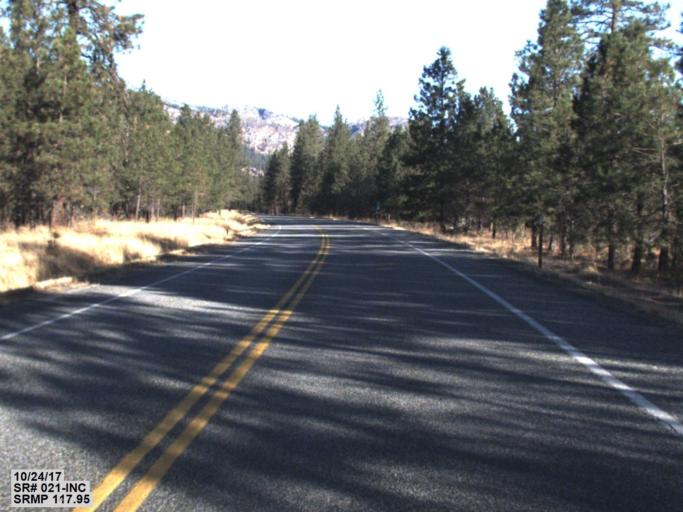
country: US
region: Washington
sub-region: Okanogan County
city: Coulee Dam
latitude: 48.0941
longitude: -118.6921
